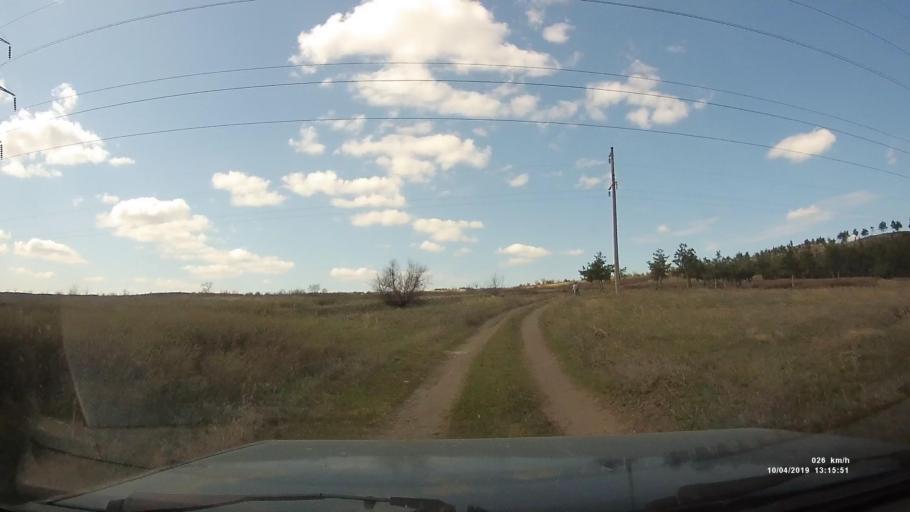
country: RU
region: Rostov
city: Masalovka
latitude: 48.4189
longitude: 40.2578
